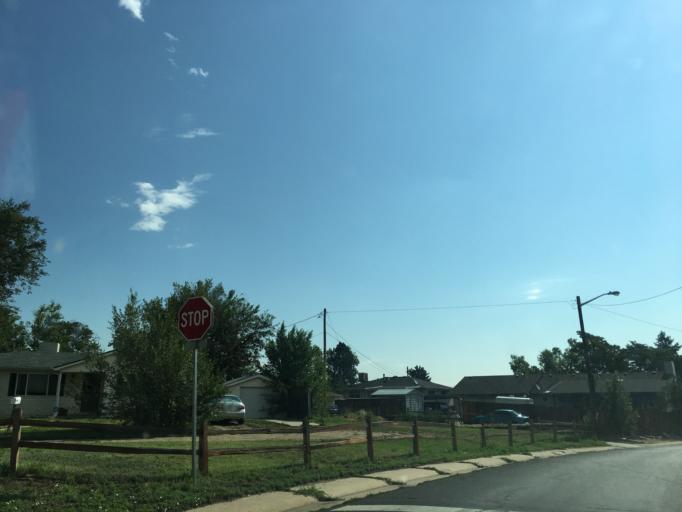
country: US
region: Colorado
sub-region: Jefferson County
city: Lakewood
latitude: 39.6972
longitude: -105.0355
